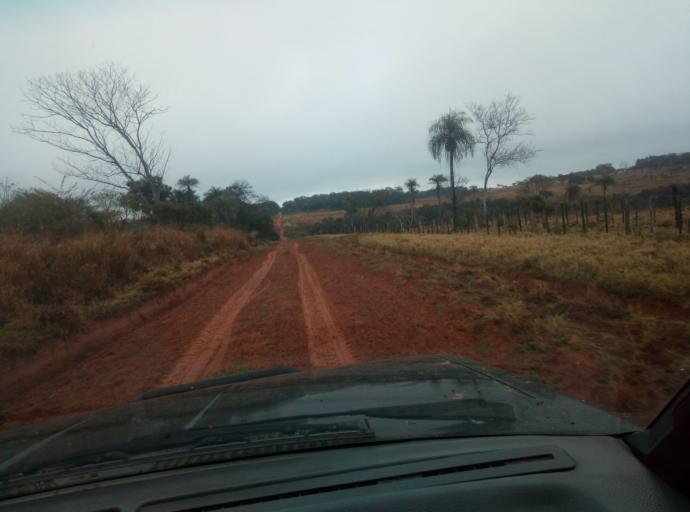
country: PY
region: Caaguazu
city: Carayao
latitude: -25.1932
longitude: -56.3318
